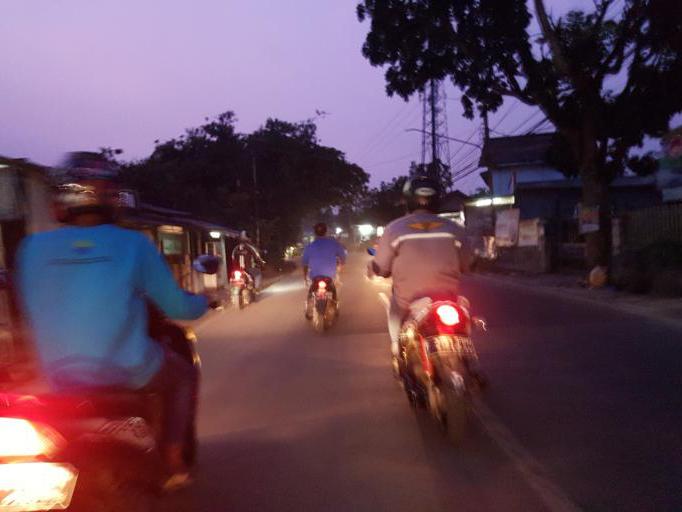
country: ID
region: West Java
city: Serpong
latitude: -6.3166
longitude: 106.6633
